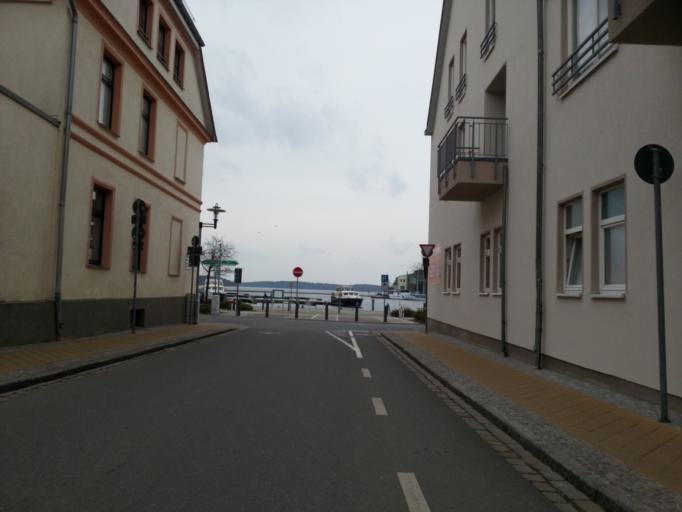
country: DE
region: Mecklenburg-Vorpommern
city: Waren
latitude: 53.5120
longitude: 12.6914
